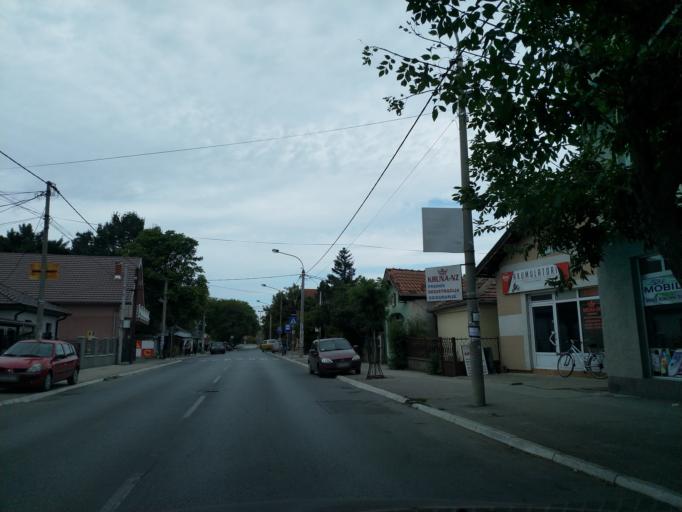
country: RS
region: Central Serbia
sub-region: Pomoravski Okrug
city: Jagodina
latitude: 43.9845
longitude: 21.2517
